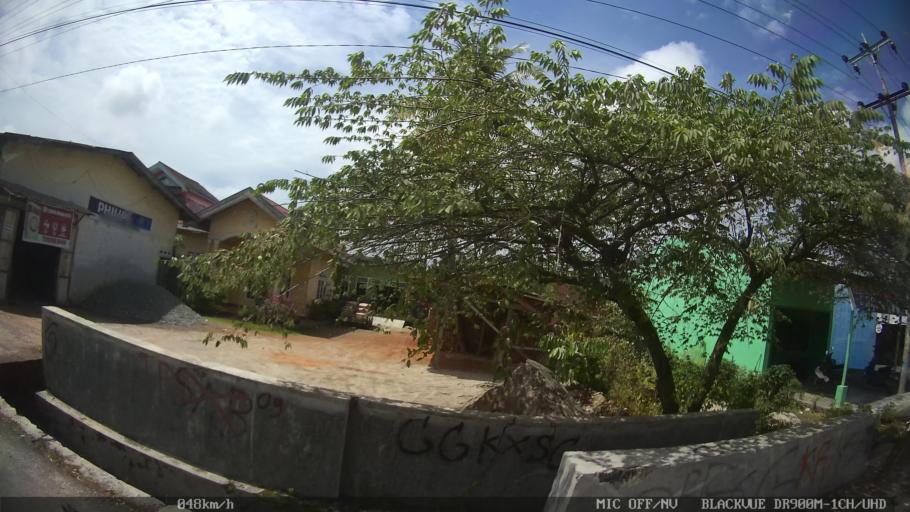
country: ID
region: North Sumatra
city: Percut
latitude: 3.6069
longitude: 98.7851
